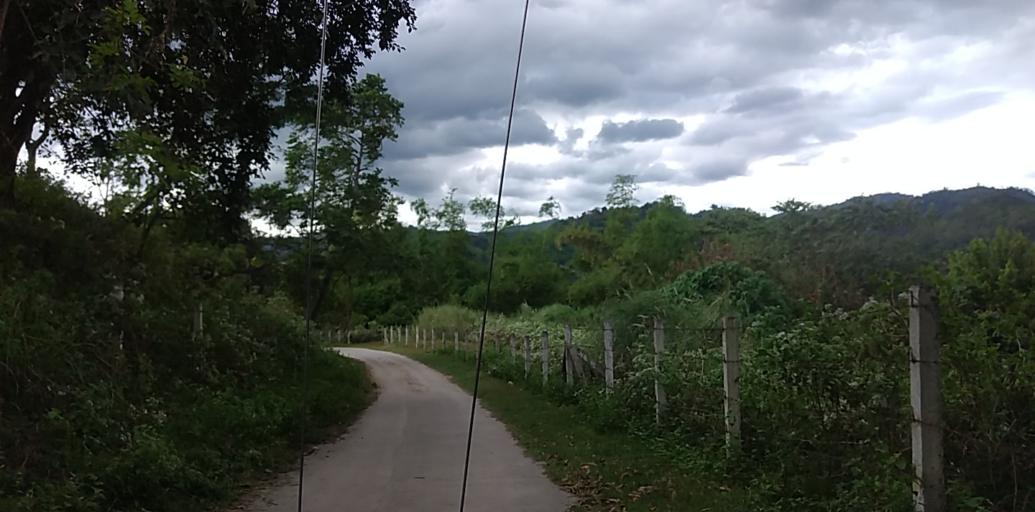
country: PH
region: Central Luzon
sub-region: Province of Pampanga
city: Babo-Pangulo
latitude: 15.1109
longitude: 120.4948
